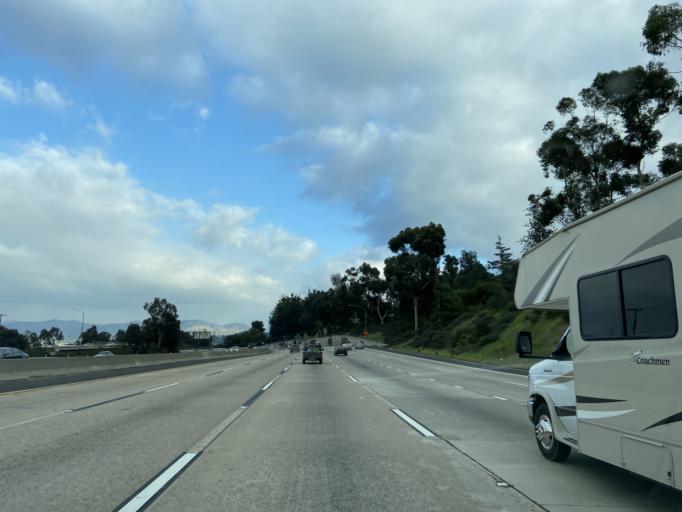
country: US
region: California
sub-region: San Diego County
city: Casa de Oro-Mount Helix
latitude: 32.7789
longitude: -116.9881
